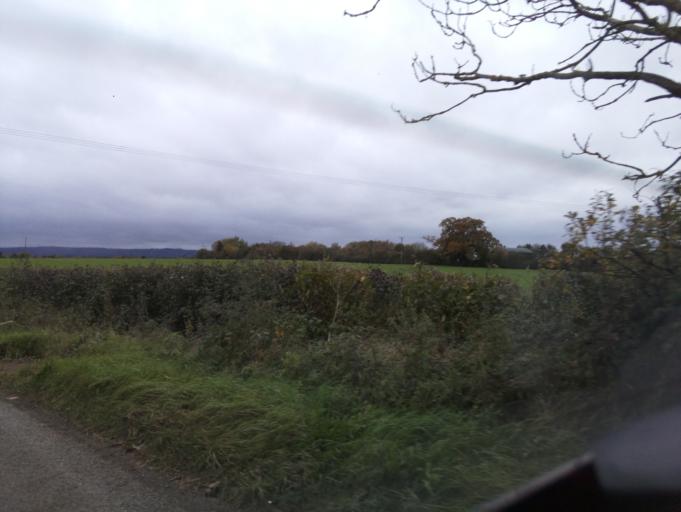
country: GB
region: England
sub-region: Somerset
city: Ilminster
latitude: 50.9538
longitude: -2.8995
